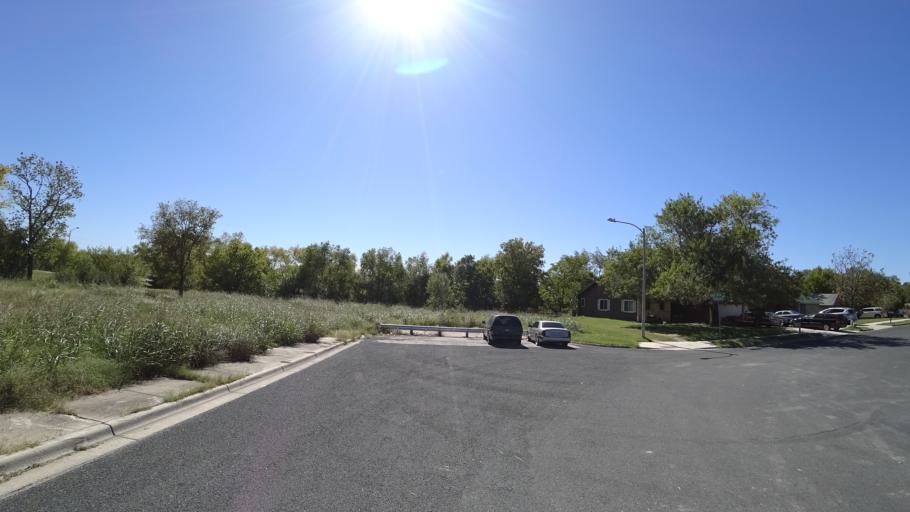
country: US
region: Texas
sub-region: Travis County
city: Hornsby Bend
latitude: 30.2973
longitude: -97.6419
